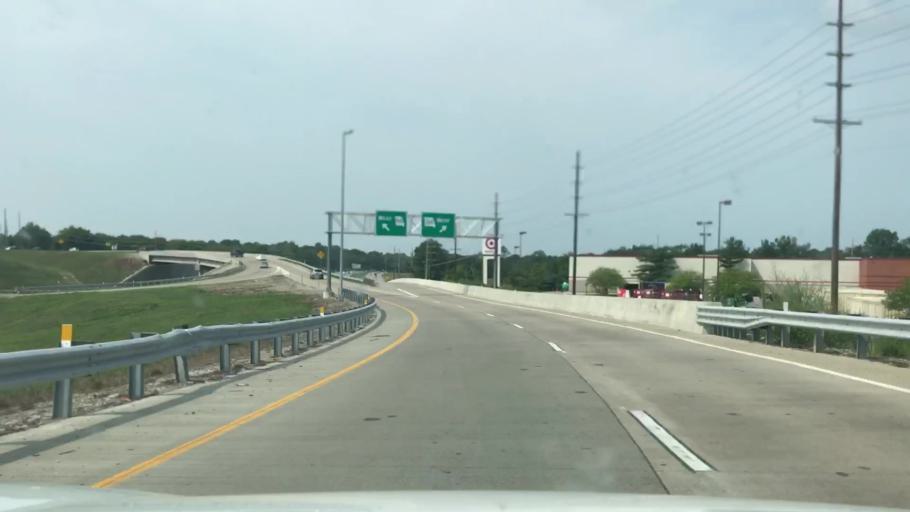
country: US
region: Missouri
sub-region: Saint Charles County
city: Cottleville
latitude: 38.7386
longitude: -90.6342
